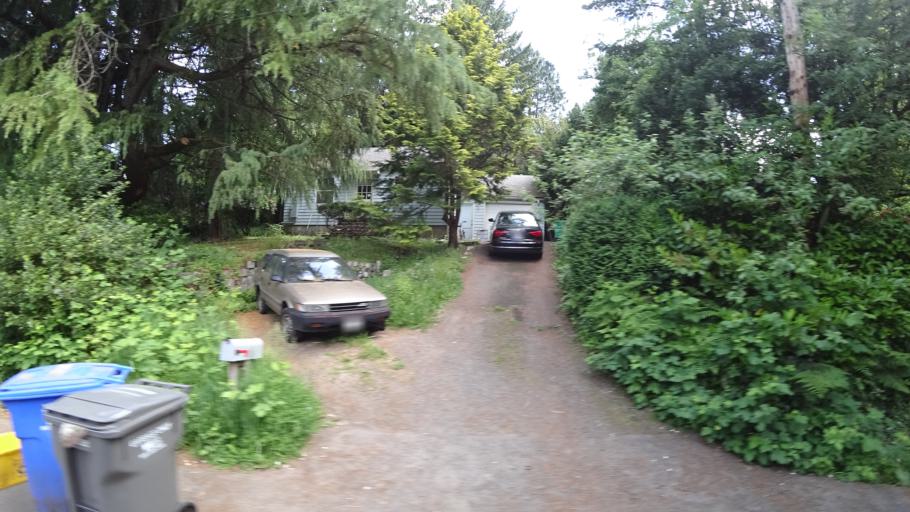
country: US
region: Oregon
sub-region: Washington County
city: Garden Home-Whitford
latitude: 45.4587
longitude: -122.7216
